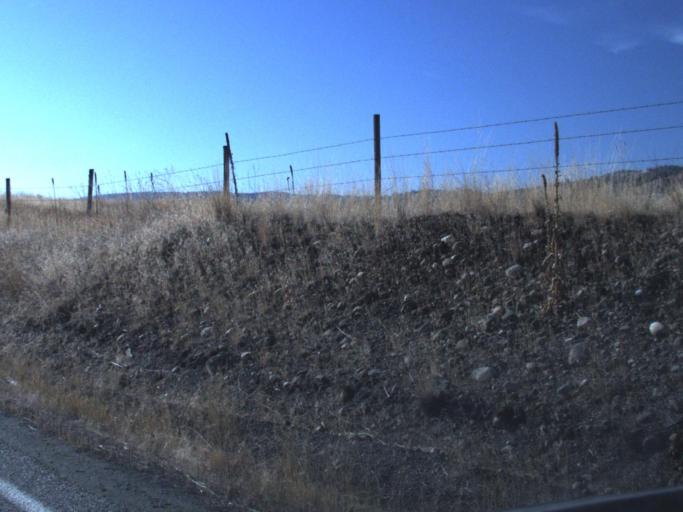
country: US
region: Washington
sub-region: Ferry County
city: Republic
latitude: 48.7639
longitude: -118.6471
